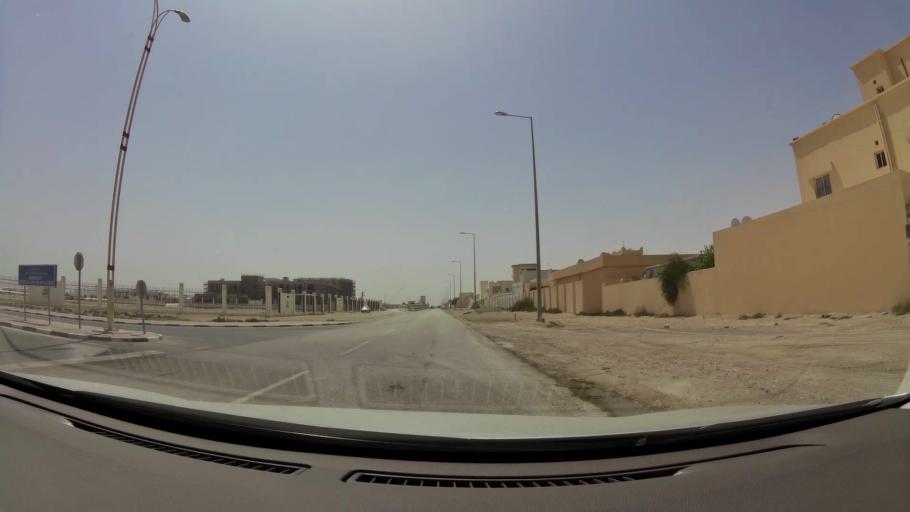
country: QA
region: Baladiyat Umm Salal
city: Umm Salal Muhammad
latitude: 25.3764
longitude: 51.4790
